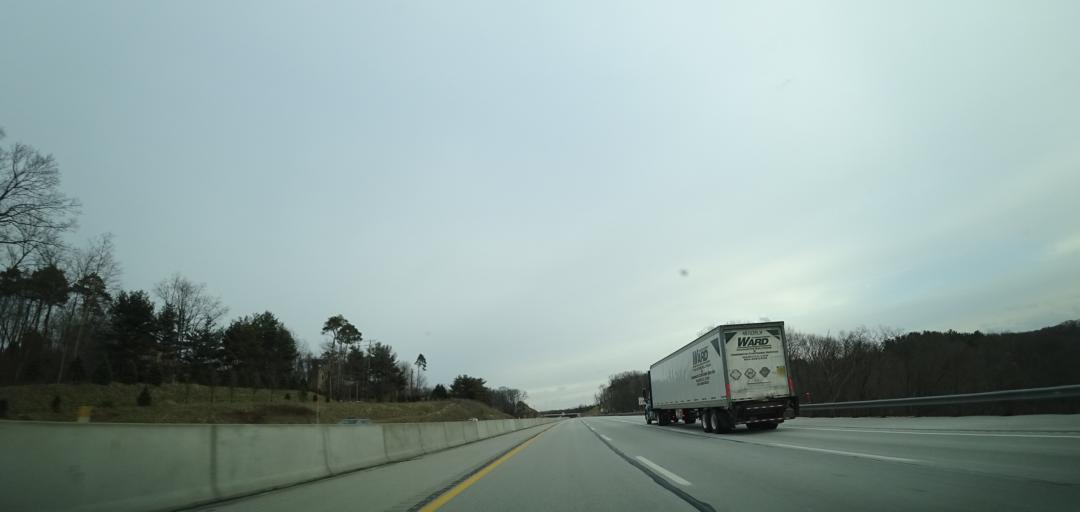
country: US
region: Pennsylvania
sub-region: Allegheny County
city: Gibsonia
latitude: 40.6434
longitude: -80.0155
